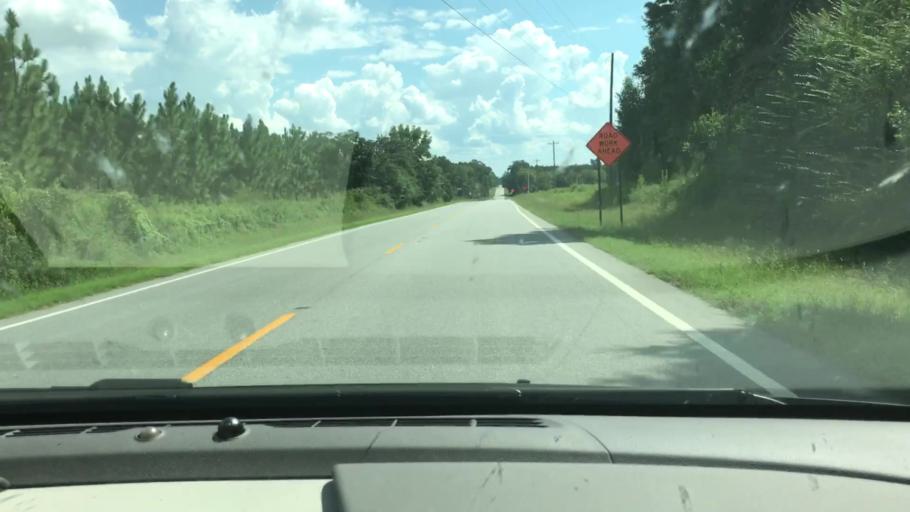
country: US
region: Georgia
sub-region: Quitman County
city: Georgetown
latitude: 31.7827
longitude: -85.0917
